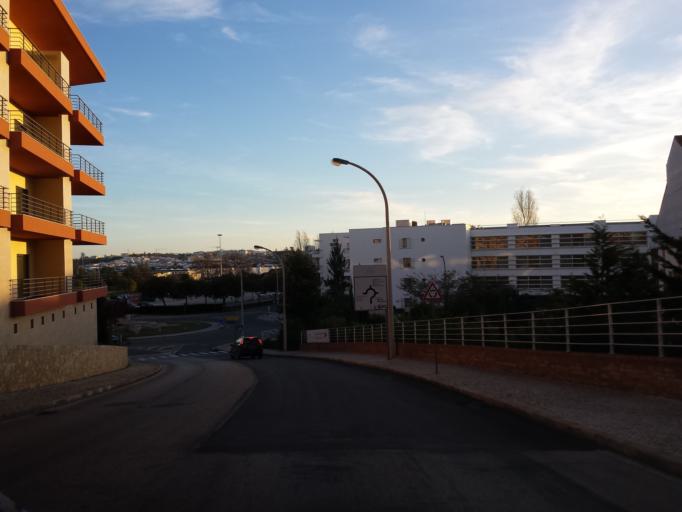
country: PT
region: Faro
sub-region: Lagos
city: Lagos
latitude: 37.1124
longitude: -8.6720
